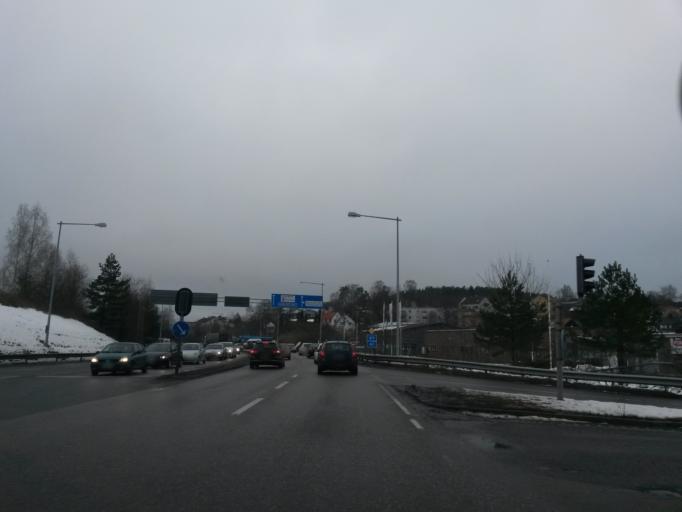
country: SE
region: Vaestra Goetaland
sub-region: Boras Kommun
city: Boras
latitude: 57.7071
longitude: 12.9499
